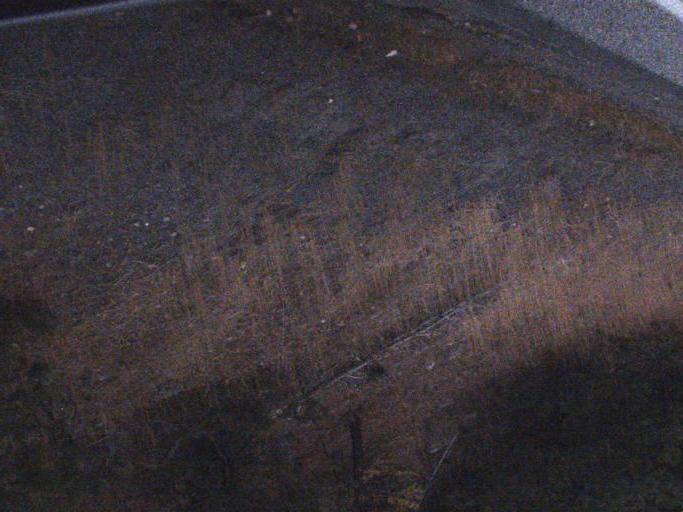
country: US
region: Washington
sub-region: Ferry County
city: Republic
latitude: 48.6109
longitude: -118.4521
